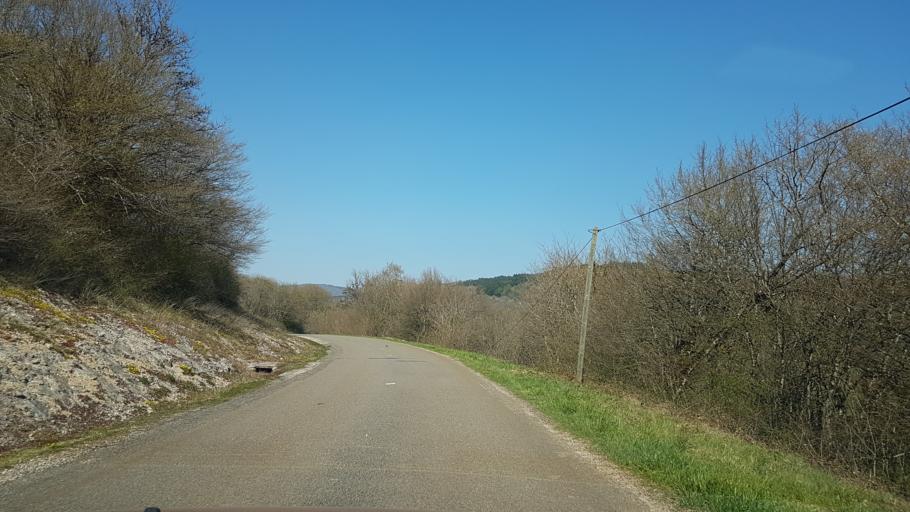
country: FR
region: Franche-Comte
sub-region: Departement du Jura
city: Orgelet
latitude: 46.5065
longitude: 5.5292
